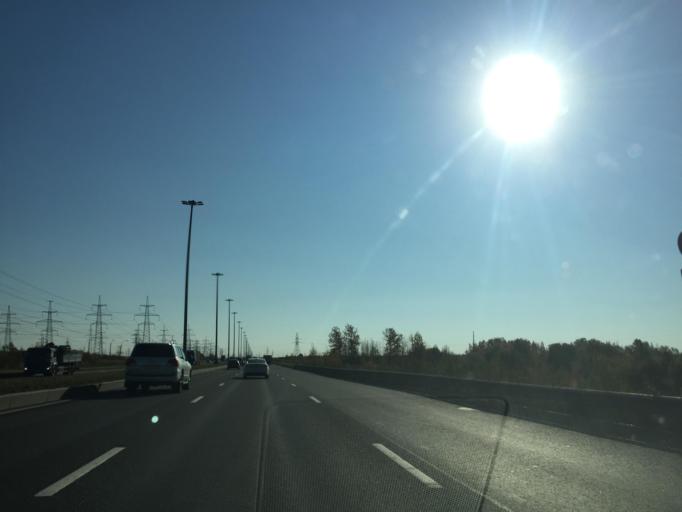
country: RU
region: St.-Petersburg
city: Petro-Slavyanka
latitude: 59.7627
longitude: 30.5079
